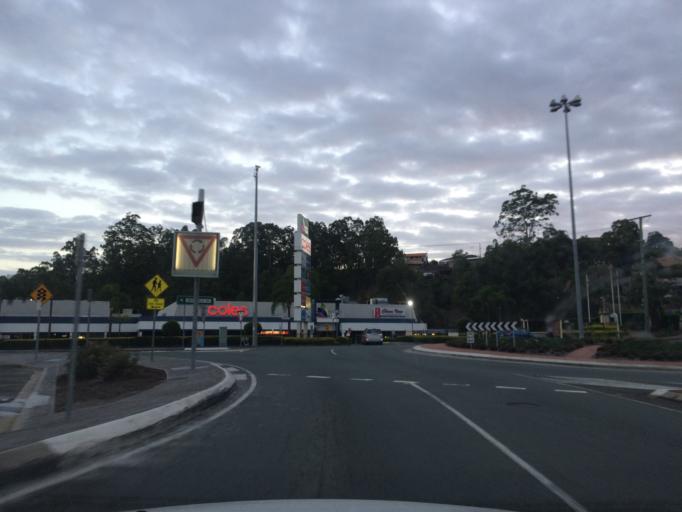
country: AU
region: Queensland
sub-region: Brisbane
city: Kenmore Hills
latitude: -27.5077
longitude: 152.9388
